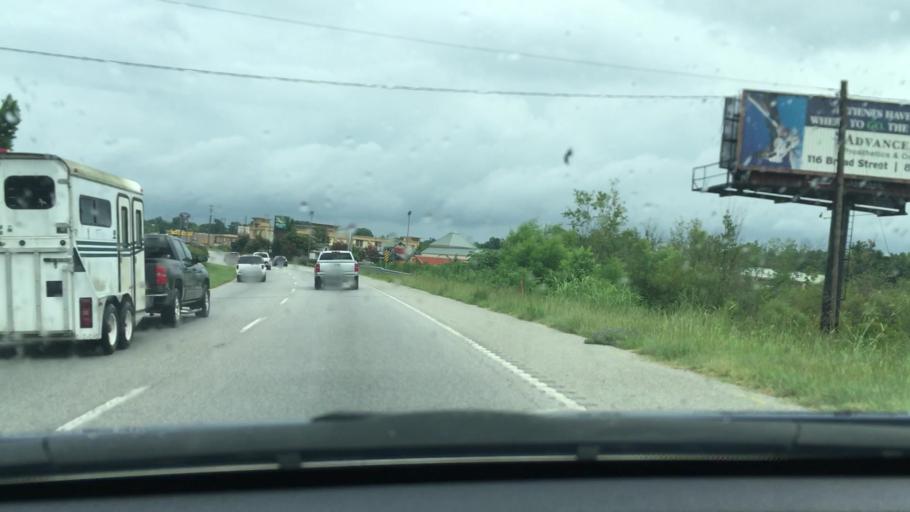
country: US
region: South Carolina
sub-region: Sumter County
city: Sumter
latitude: 33.9576
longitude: -80.3939
